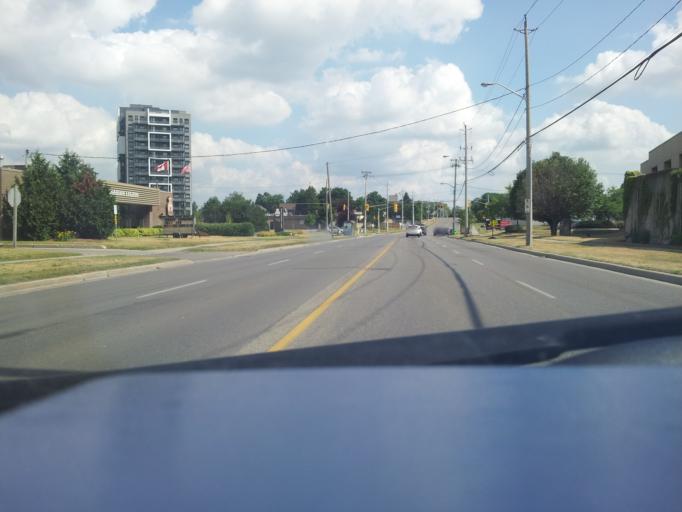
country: CA
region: Ontario
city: Waterloo
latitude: 43.4484
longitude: -80.5147
